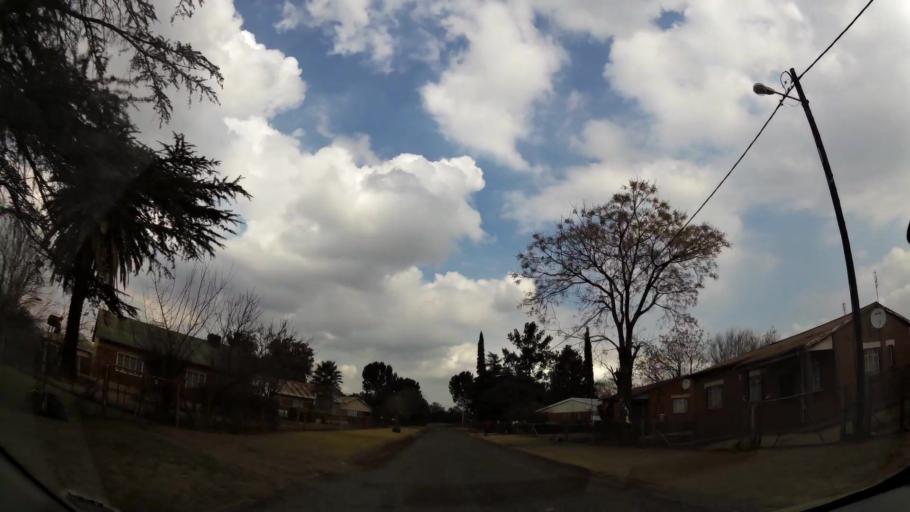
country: ZA
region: Gauteng
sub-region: Sedibeng District Municipality
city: Vereeniging
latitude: -26.6750
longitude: 27.9368
